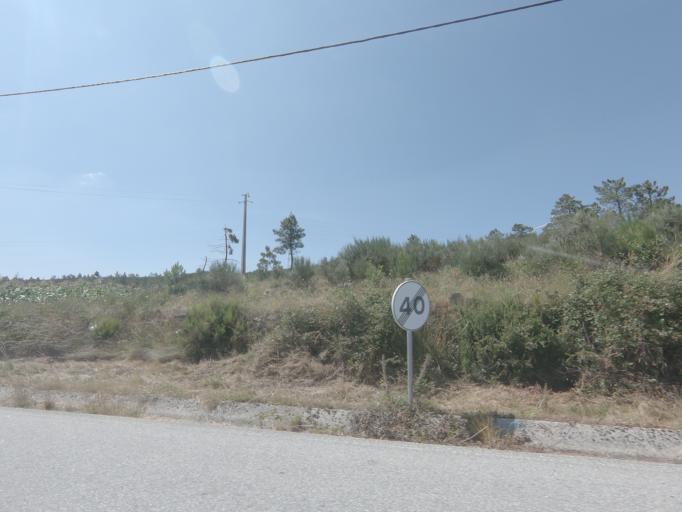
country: PT
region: Viseu
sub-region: Tarouca
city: Tarouca
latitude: 40.9849
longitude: -7.7844
